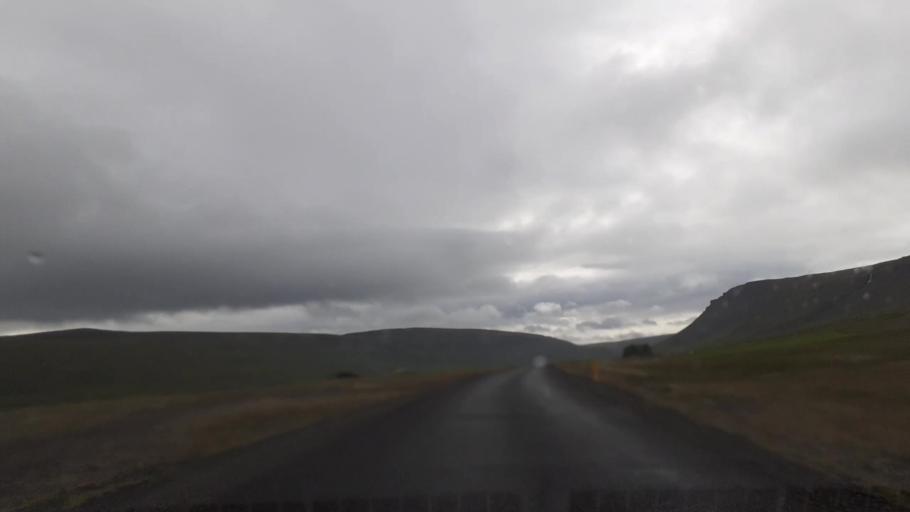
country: IS
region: East
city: Egilsstadir
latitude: 65.6207
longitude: -15.0866
